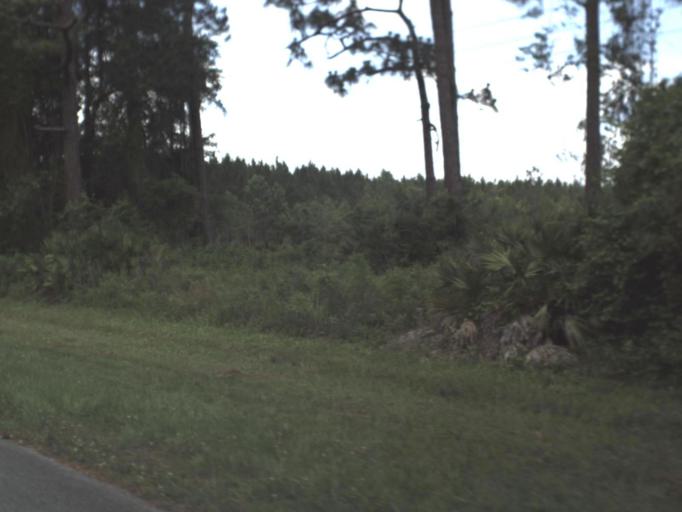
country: US
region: Florida
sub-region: Nassau County
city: Yulee
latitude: 30.6794
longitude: -81.6474
